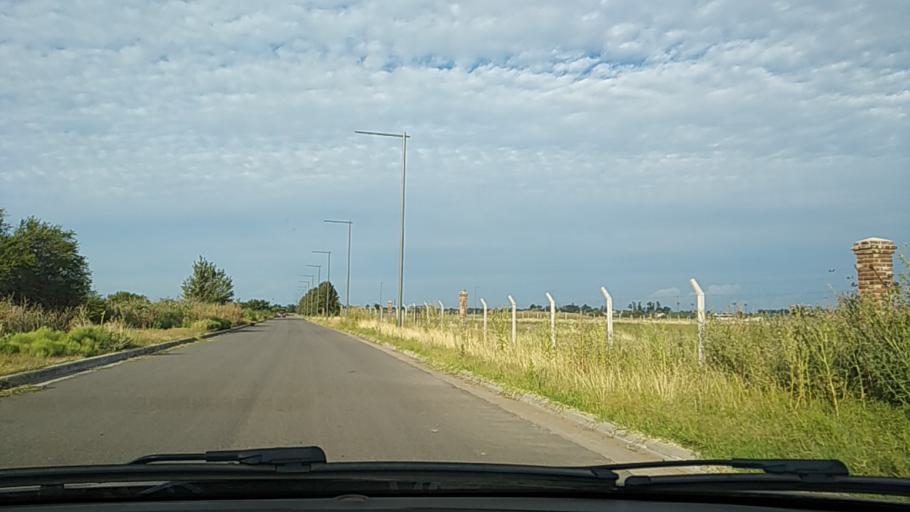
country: AR
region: Santa Fe
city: Funes
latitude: -32.9425
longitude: -60.7742
